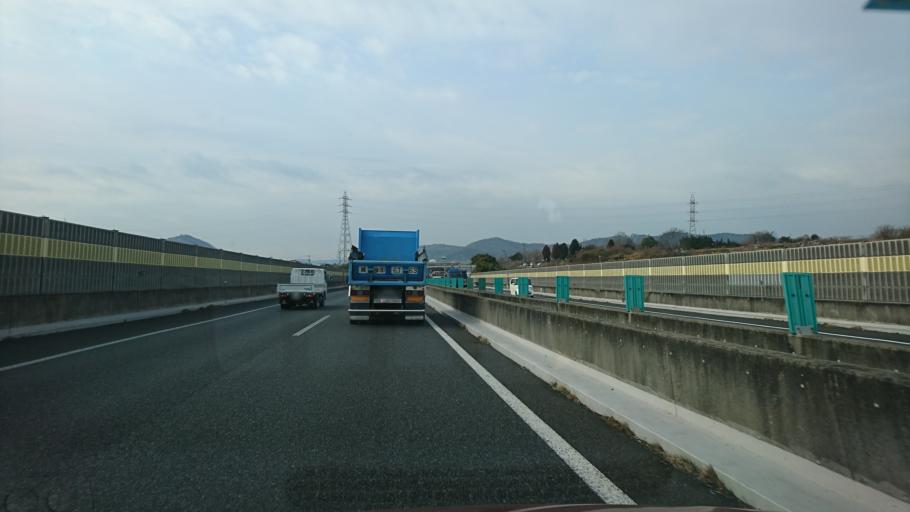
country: JP
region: Okayama
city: Okayama-shi
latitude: 34.6958
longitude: 133.8788
